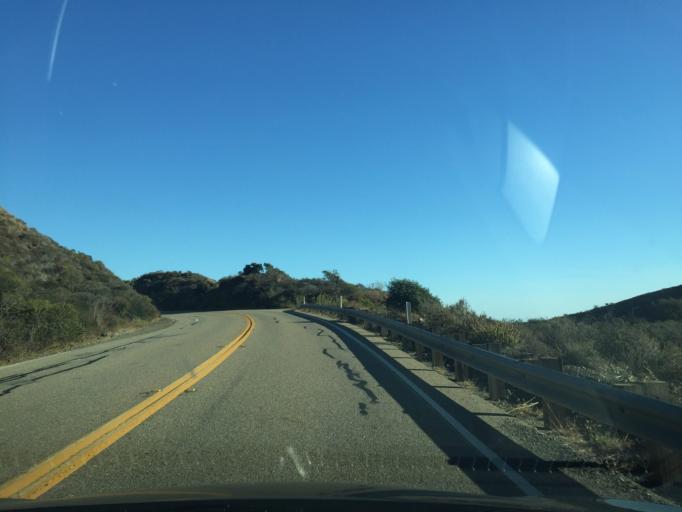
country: US
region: California
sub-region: San Luis Obispo County
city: Cambria
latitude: 35.8239
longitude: -121.3808
